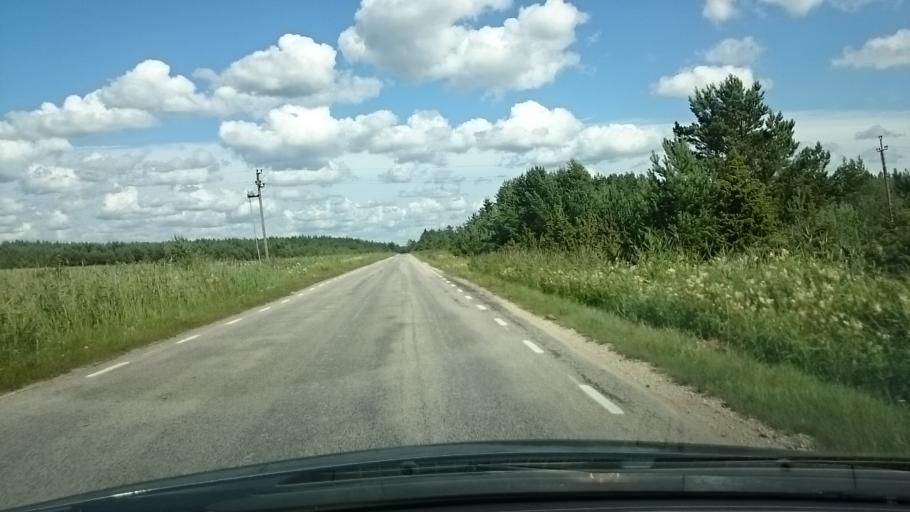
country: EE
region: Laeaene
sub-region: Haapsalu linn
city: Haapsalu
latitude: 59.0495
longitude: 23.5191
